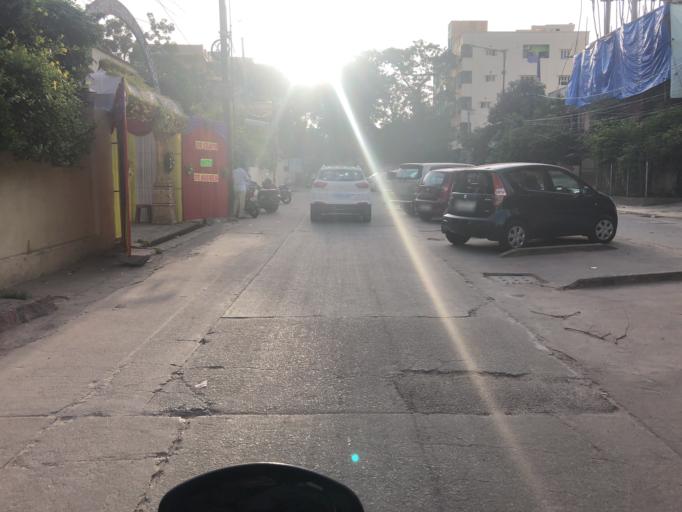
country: IN
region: Telangana
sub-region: Rangareddi
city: Kukatpalli
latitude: 17.4391
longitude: 78.4365
